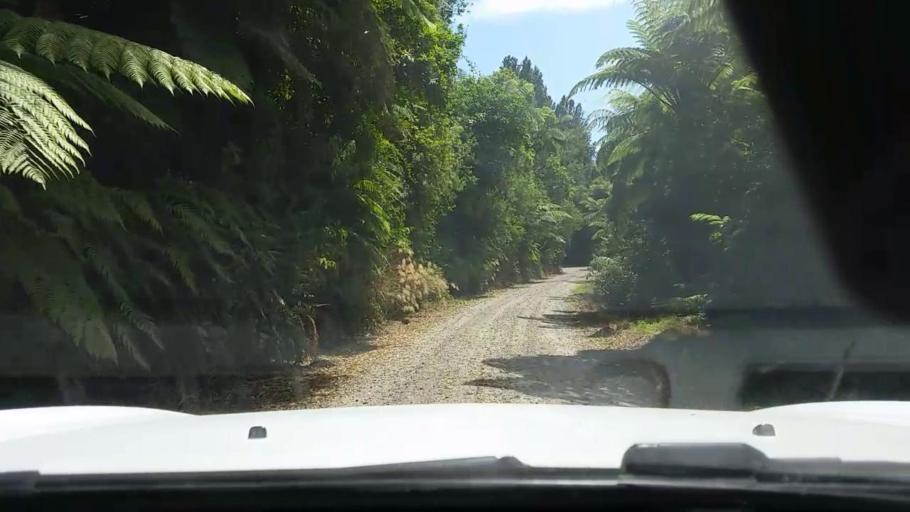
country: NZ
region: Bay of Plenty
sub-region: Rotorua District
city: Rotorua
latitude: -37.9656
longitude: 176.3060
